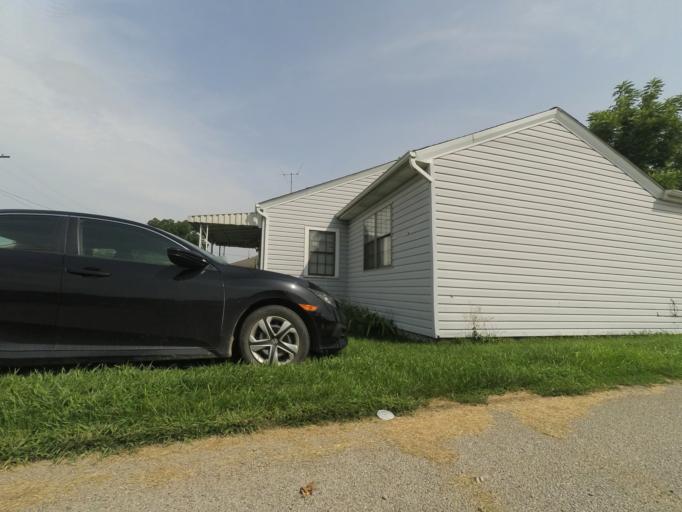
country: US
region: West Virginia
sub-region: Cabell County
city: Huntington
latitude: 38.4085
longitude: -82.4709
